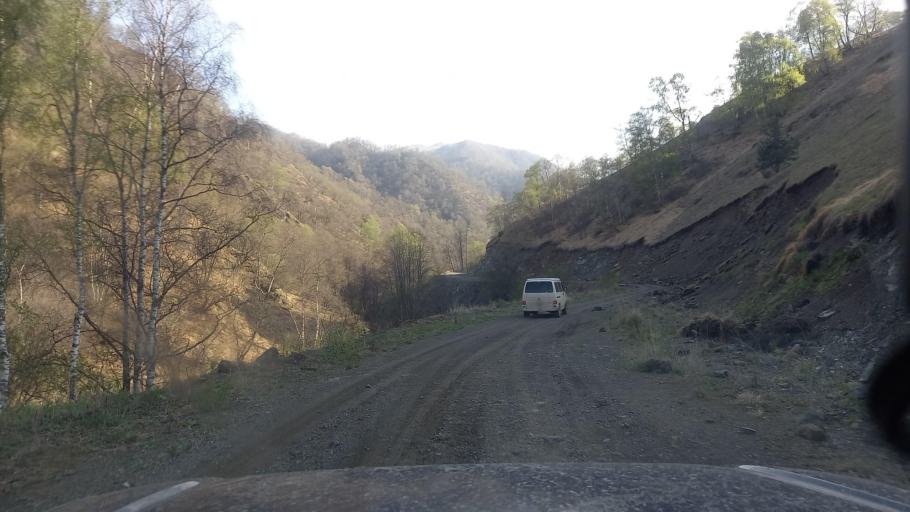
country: RU
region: Kabardino-Balkariya
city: Kamennomostskoye
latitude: 43.7021
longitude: 42.8438
